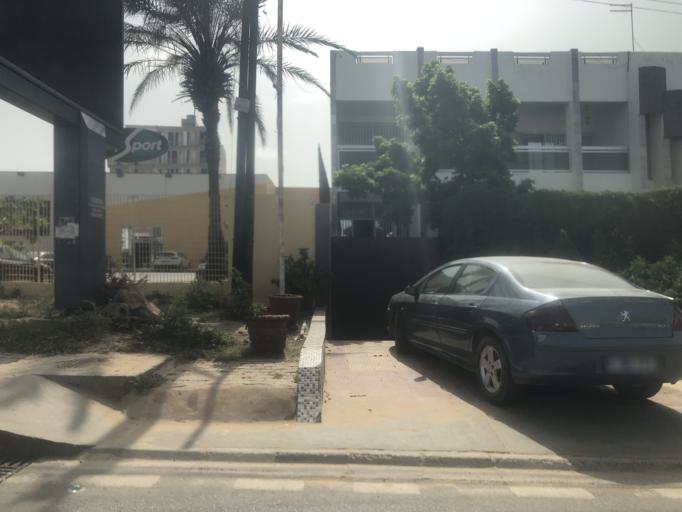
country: SN
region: Dakar
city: Mermoz Boabab
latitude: 14.7417
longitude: -17.5109
